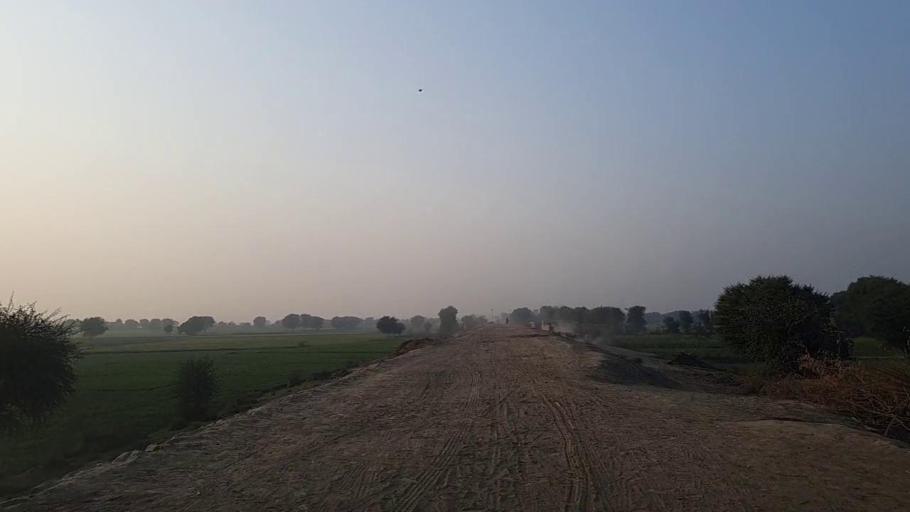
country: PK
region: Sindh
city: Sann
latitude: 26.1719
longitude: 68.1040
